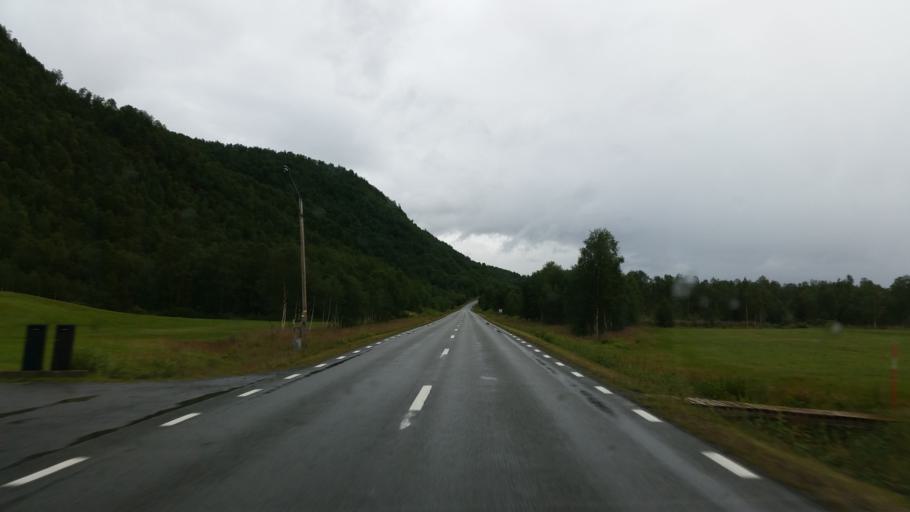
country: NO
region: Nordland
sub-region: Rana
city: Mo i Rana
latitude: 65.8789
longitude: 14.9976
